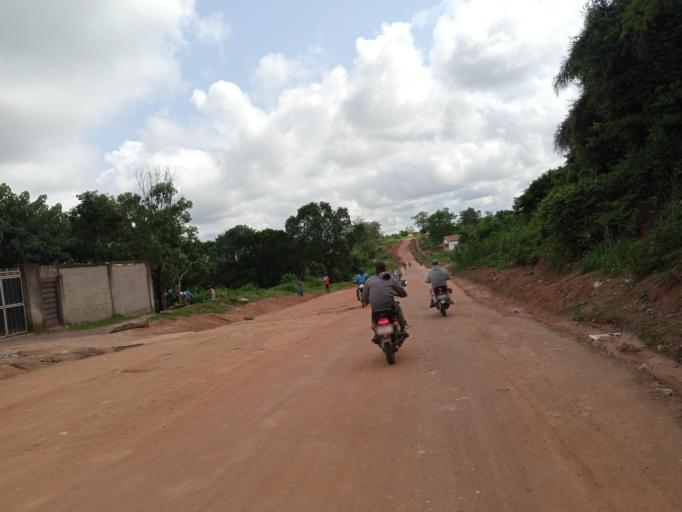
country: SL
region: Southern Province
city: Bo
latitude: 7.9864
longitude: -11.7372
